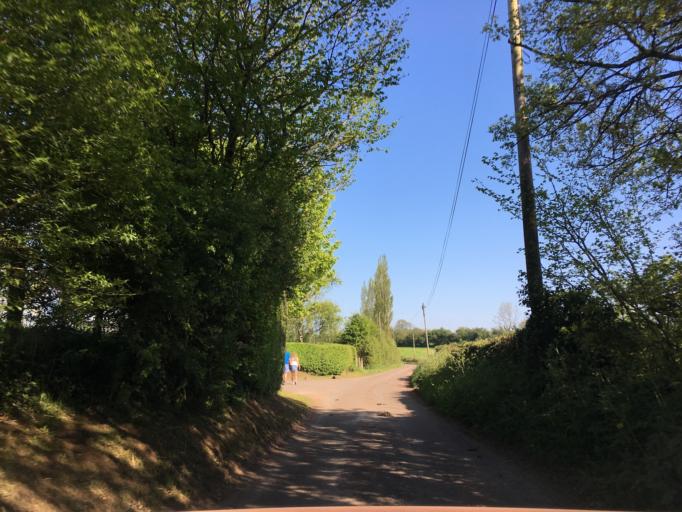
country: GB
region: Wales
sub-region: Monmouthshire
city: Caldicot
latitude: 51.6389
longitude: -2.7374
